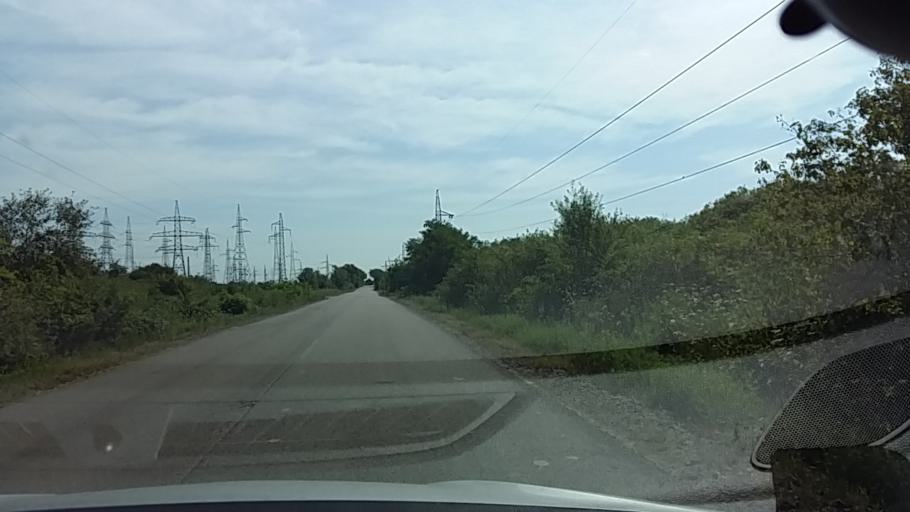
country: HU
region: Heves
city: Domoszlo
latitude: 47.7720
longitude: 20.1015
